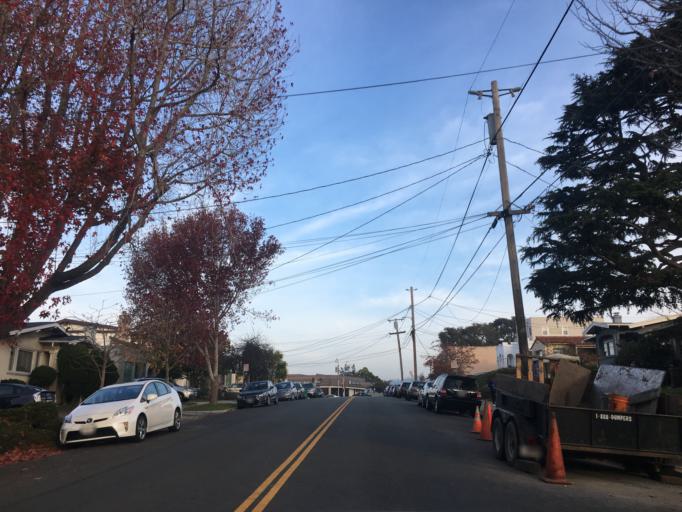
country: US
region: California
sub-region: Alameda County
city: Albany
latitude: 37.8898
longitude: -122.2885
